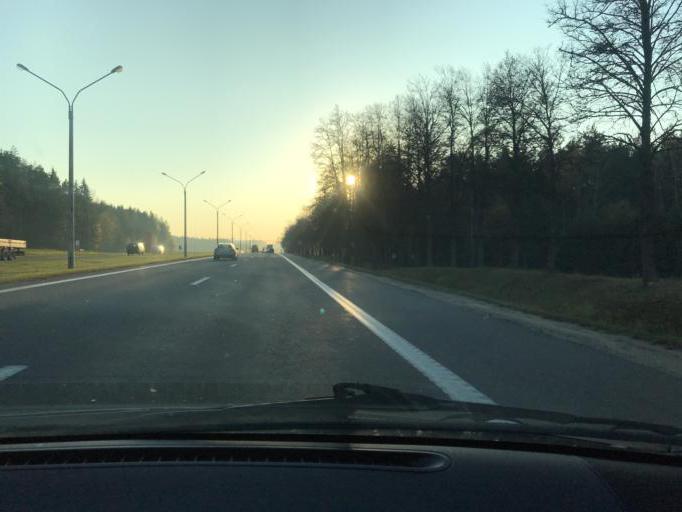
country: BY
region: Minsk
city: Korolev Stan
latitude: 53.9829
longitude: 27.7830
